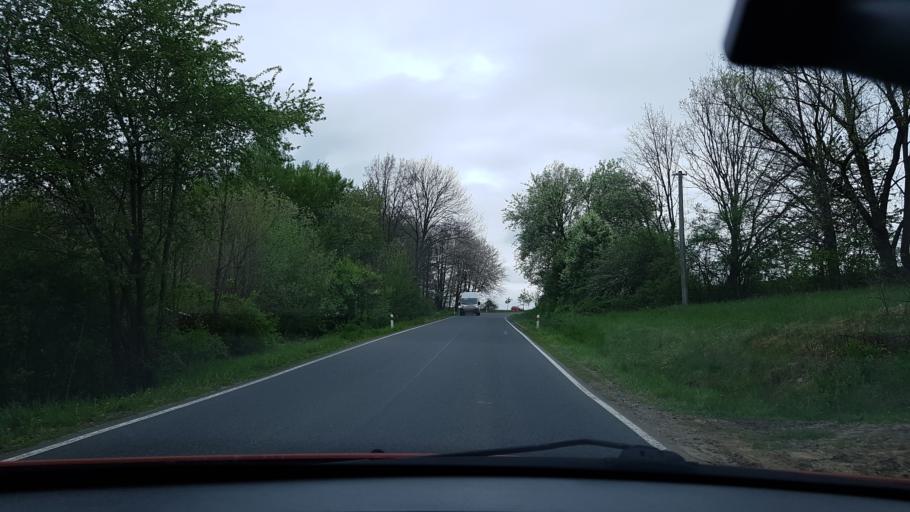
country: CZ
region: Olomoucky
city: Mikulovice
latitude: 50.3065
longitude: 17.3185
